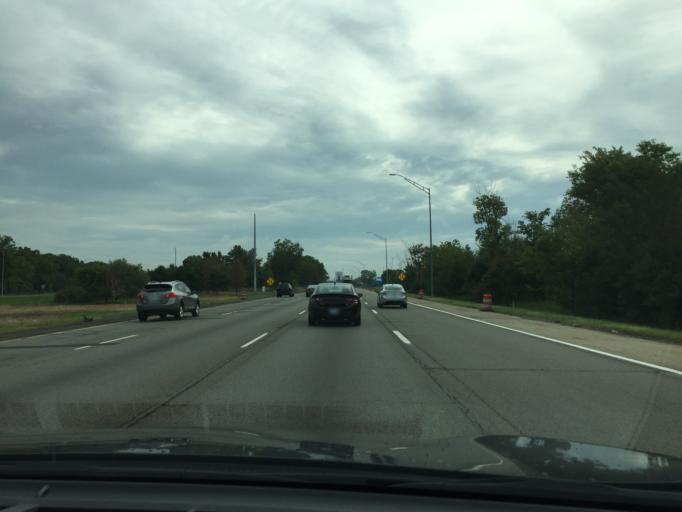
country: US
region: Michigan
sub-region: Wayne County
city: Taylor
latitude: 42.2452
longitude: -83.3158
